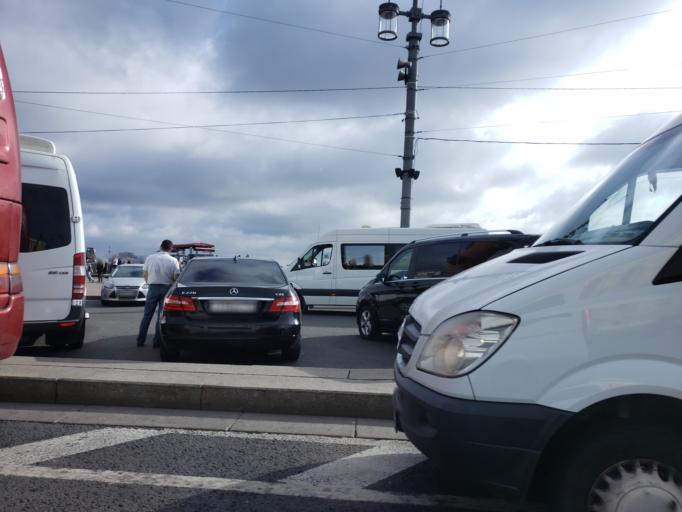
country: RU
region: St.-Petersburg
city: Saint Petersburg
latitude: 59.9428
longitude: 30.3066
